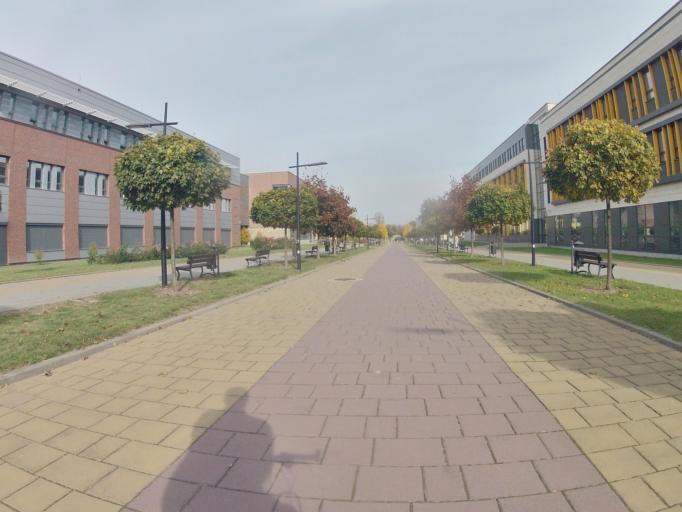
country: PL
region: Lesser Poland Voivodeship
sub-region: Krakow
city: Krakow
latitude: 50.0283
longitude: 19.9054
